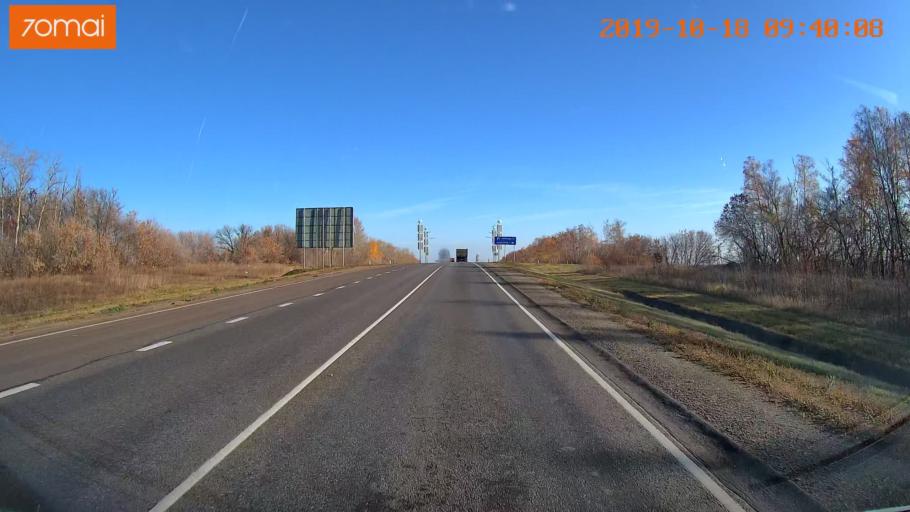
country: RU
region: Tula
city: Yefremov
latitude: 53.2606
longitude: 38.1440
